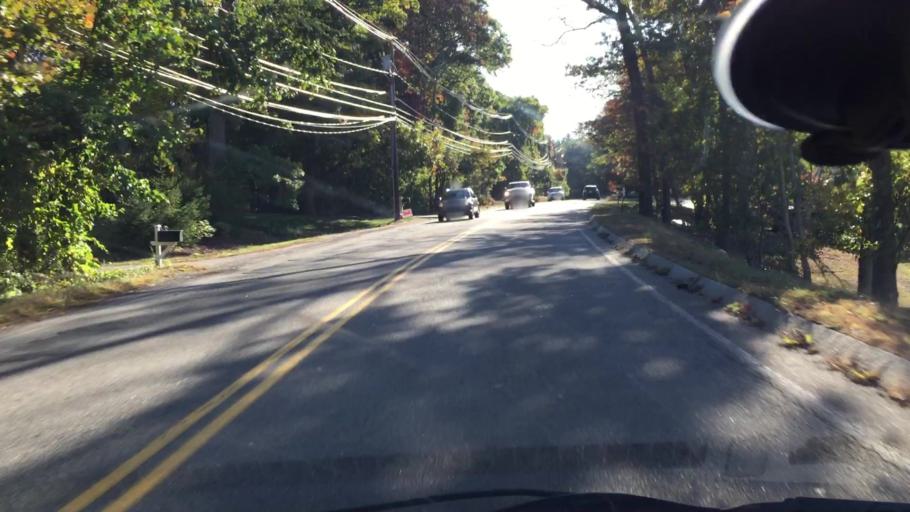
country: US
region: Massachusetts
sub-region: Norfolk County
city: Westwood
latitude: 42.2037
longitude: -71.2569
